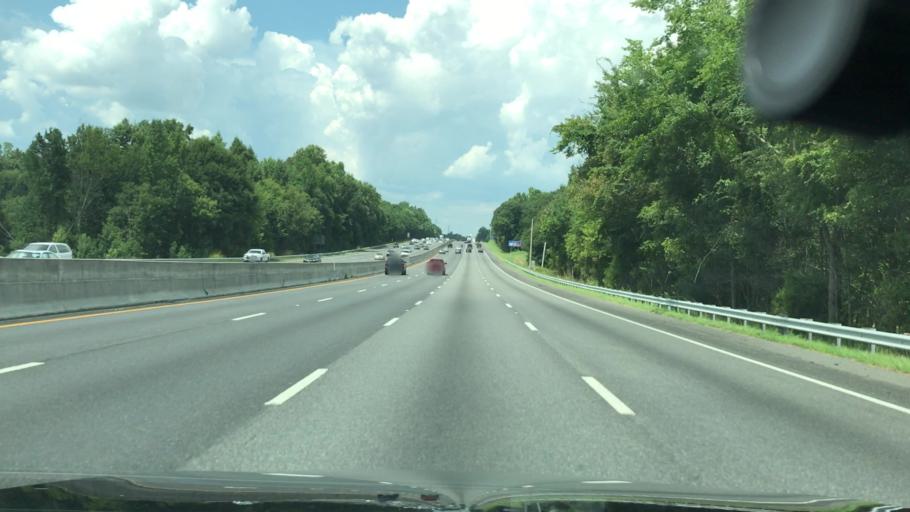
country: US
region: South Carolina
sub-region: York County
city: Fort Mill
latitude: 35.0461
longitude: -80.9591
